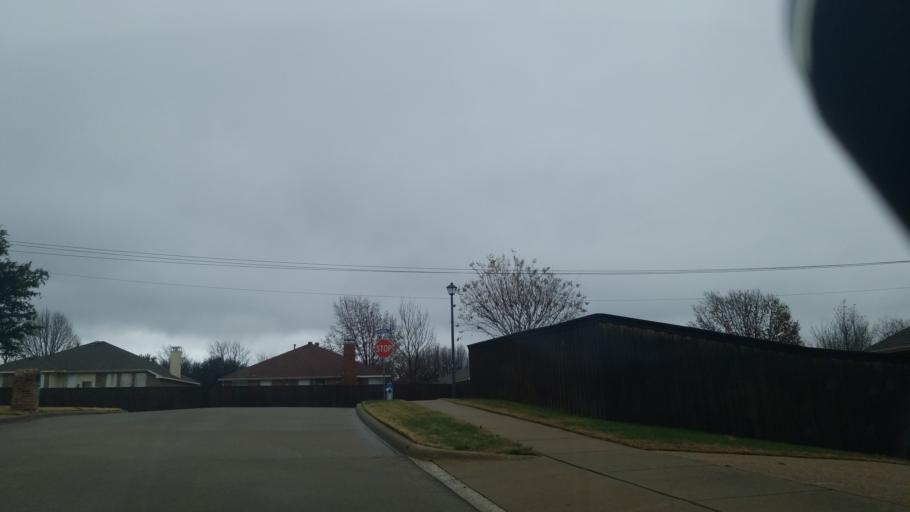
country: US
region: Texas
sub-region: Denton County
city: Corinth
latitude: 33.1394
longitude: -97.0885
